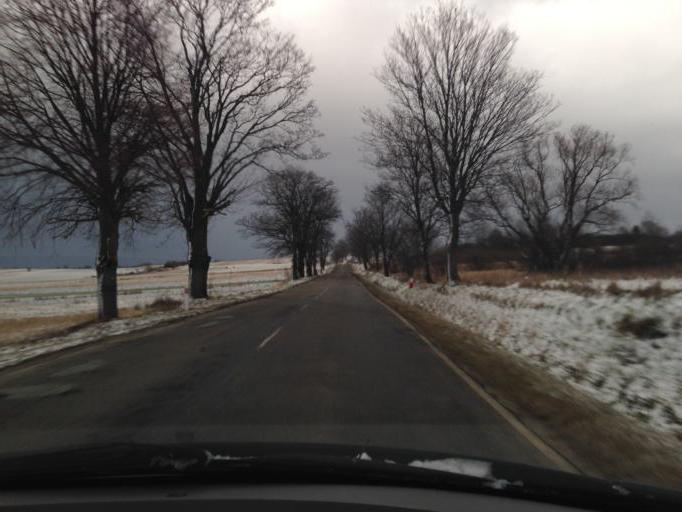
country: PL
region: Subcarpathian Voivodeship
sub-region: Powiat jasielski
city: Osiek Jasielski
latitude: 49.6103
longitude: 21.4951
